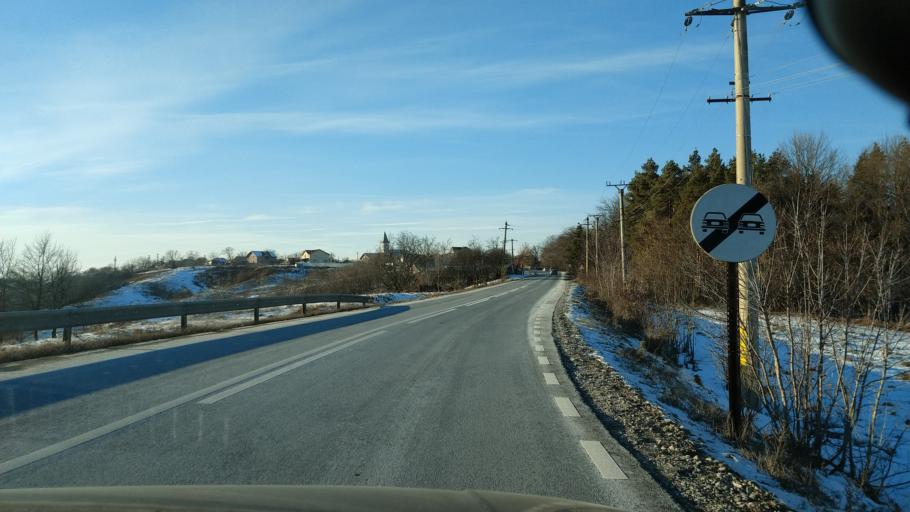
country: RO
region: Bacau
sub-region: Comuna Sanduleni
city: Sanduleni
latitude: 46.4921
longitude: 26.7783
